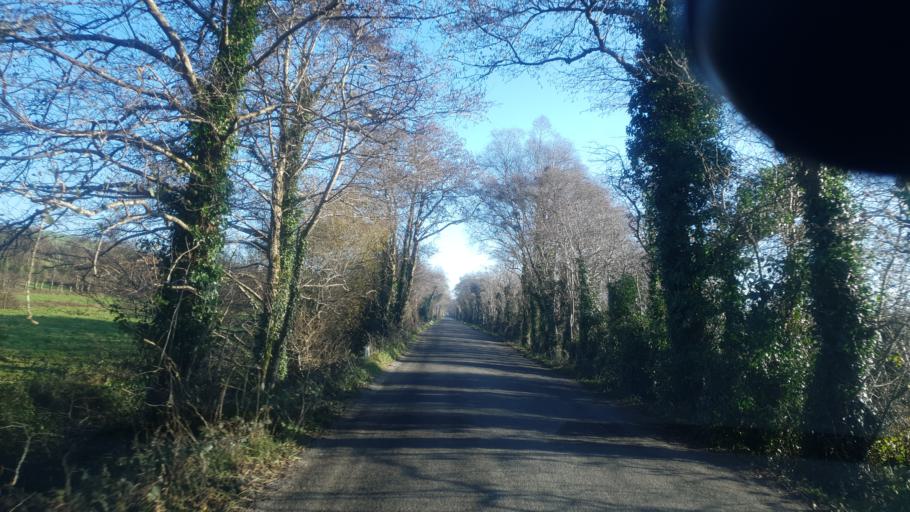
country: IE
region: Munster
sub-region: Ciarrai
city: Cill Airne
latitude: 52.1082
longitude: -9.4782
